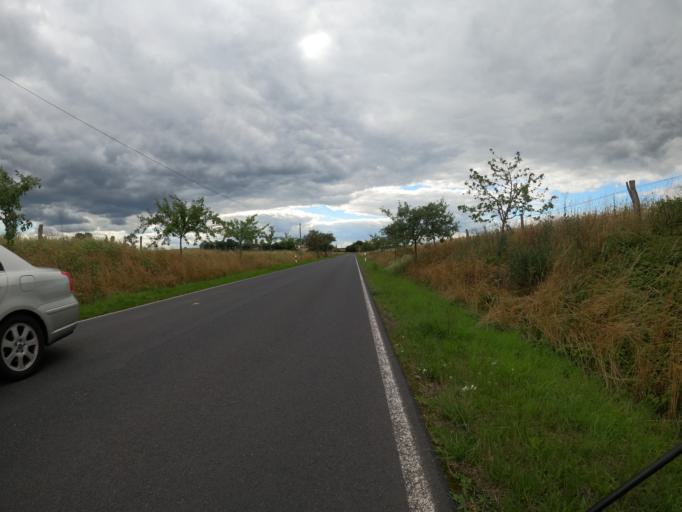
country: DE
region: Brandenburg
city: Angermunde
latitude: 53.0371
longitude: 13.9821
